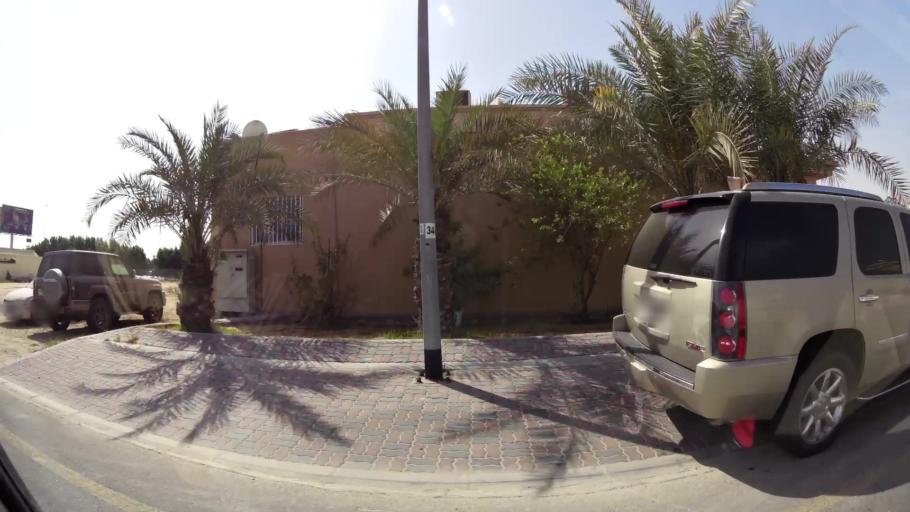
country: AE
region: Ash Shariqah
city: Sharjah
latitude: 25.2692
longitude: 55.4130
